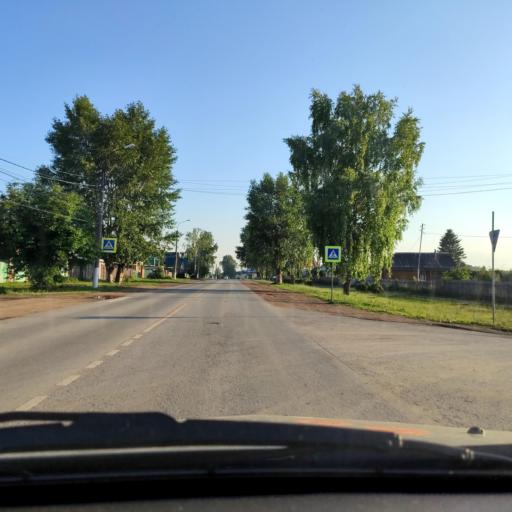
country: RU
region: Bashkortostan
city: Blagoveshchensk
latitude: 55.0390
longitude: 55.9975
